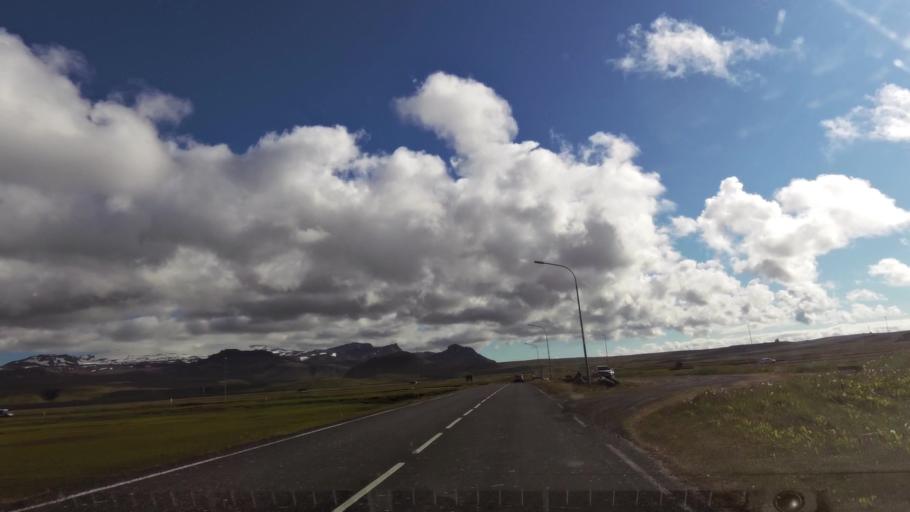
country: IS
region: West
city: Olafsvik
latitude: 64.9205
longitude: -23.8192
